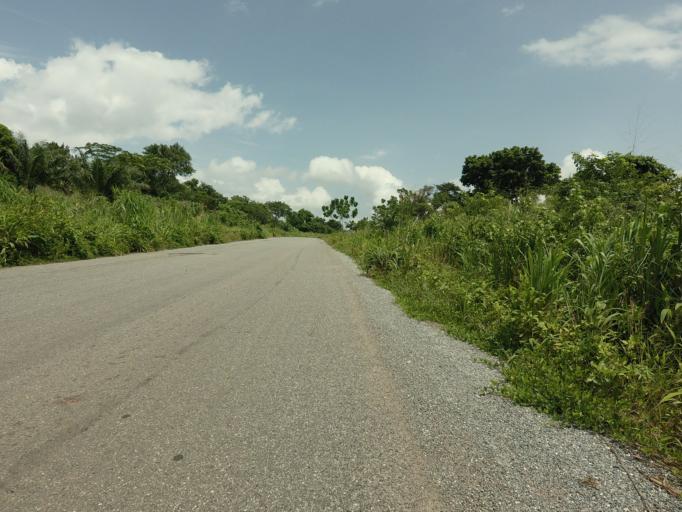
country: GH
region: Volta
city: Kpandu
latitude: 6.8681
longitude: 0.4119
